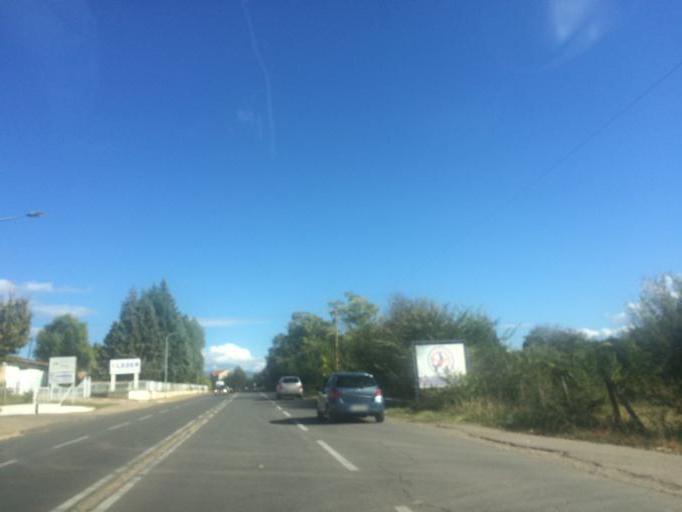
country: MK
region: Kocani
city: Orizari
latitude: 41.9136
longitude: 22.4337
